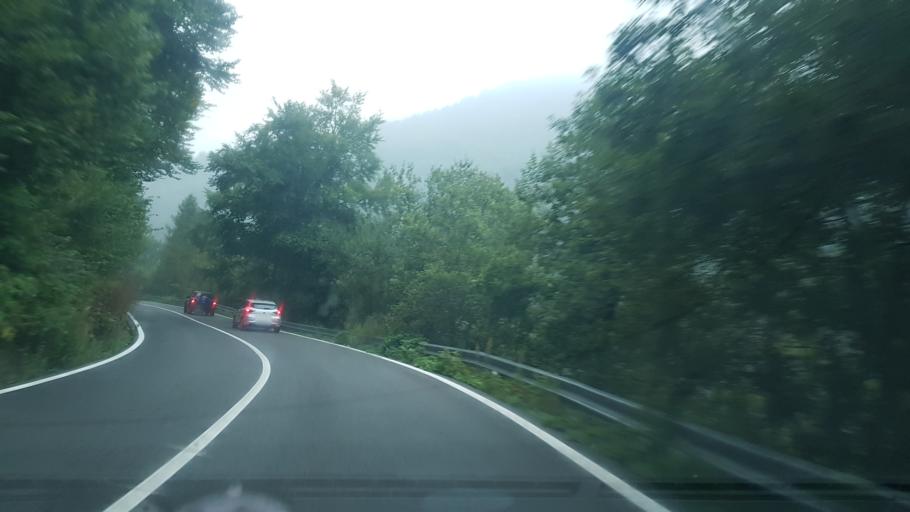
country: IT
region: Piedmont
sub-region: Provincia di Cuneo
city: Frabosa Soprana
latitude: 44.2622
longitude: 7.7677
